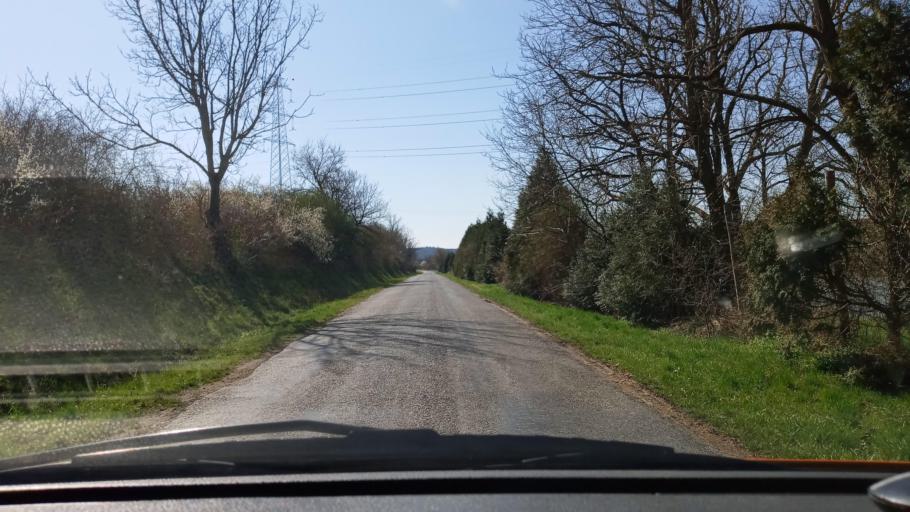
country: HU
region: Baranya
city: Kozarmisleny
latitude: 46.0464
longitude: 18.3823
